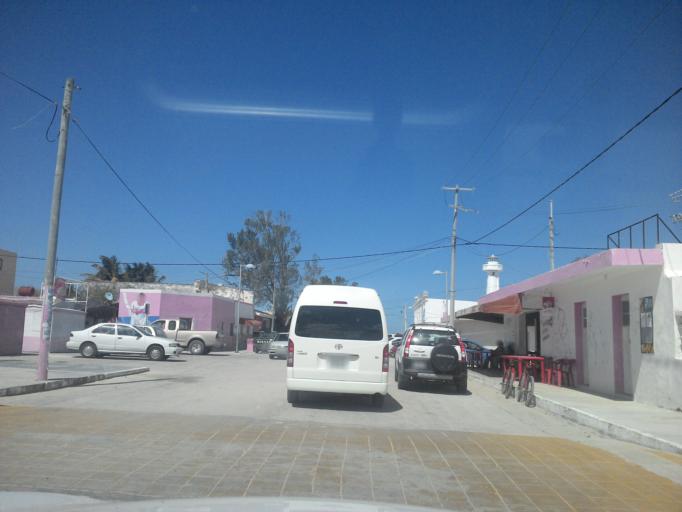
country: MX
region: Yucatan
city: Telchac Puerto
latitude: 21.3427
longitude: -89.2637
